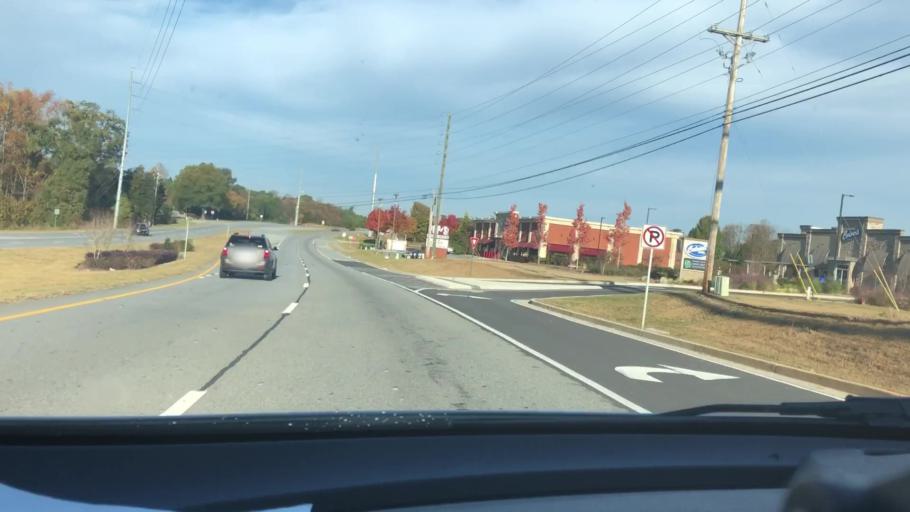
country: US
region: Georgia
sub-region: Fulton County
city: Johns Creek
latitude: 34.0861
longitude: -84.1630
